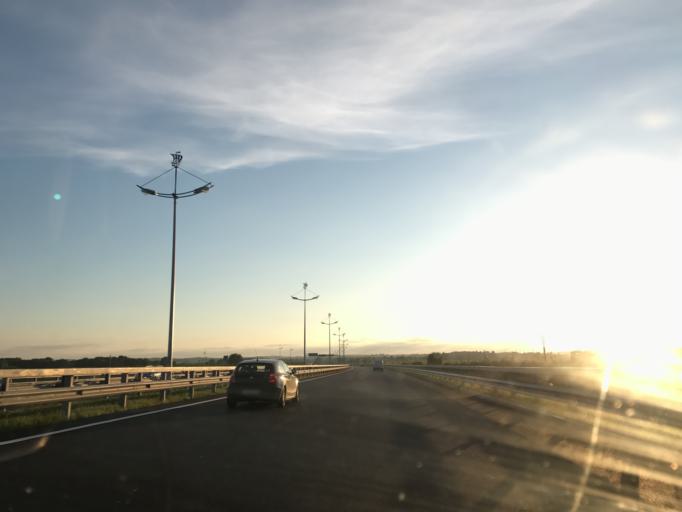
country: RU
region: Kaliningrad
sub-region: Zelenogradskiy Rayon
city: Zelenogradsk
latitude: 54.9234
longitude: 20.3986
